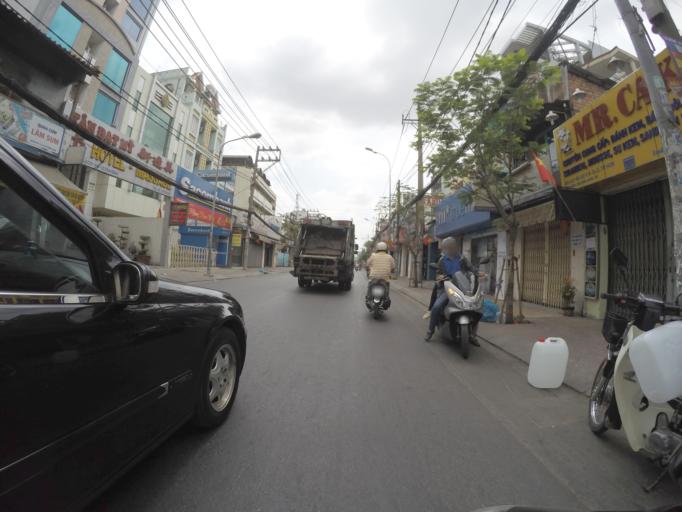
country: VN
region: Ho Chi Minh City
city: Quan Muoi Mot
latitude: 10.7739
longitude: 106.6485
